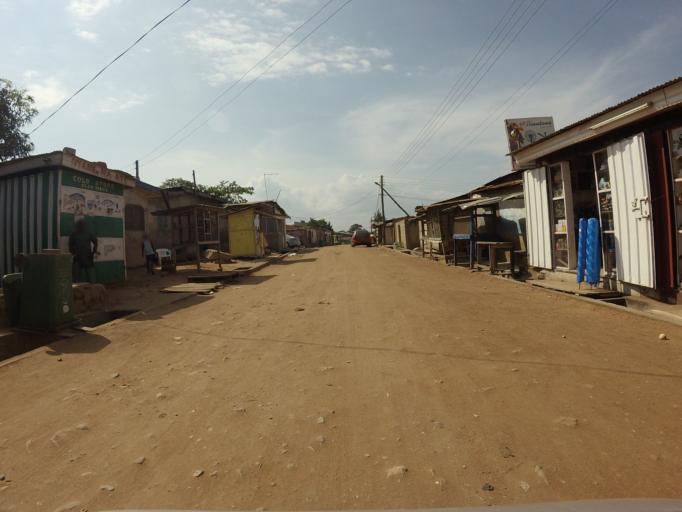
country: GH
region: Greater Accra
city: Dome
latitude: 5.6284
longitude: -0.2315
